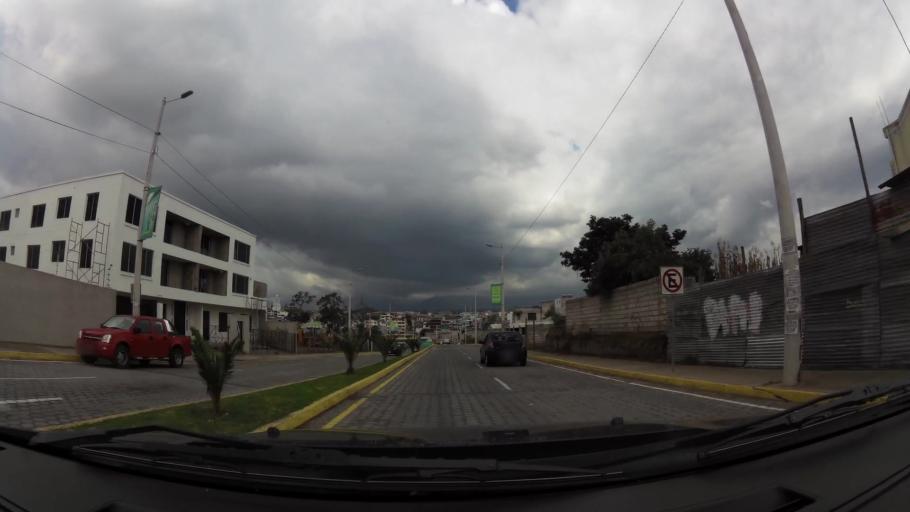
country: EC
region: Pichincha
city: Sangolqui
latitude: -0.3299
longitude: -78.4533
